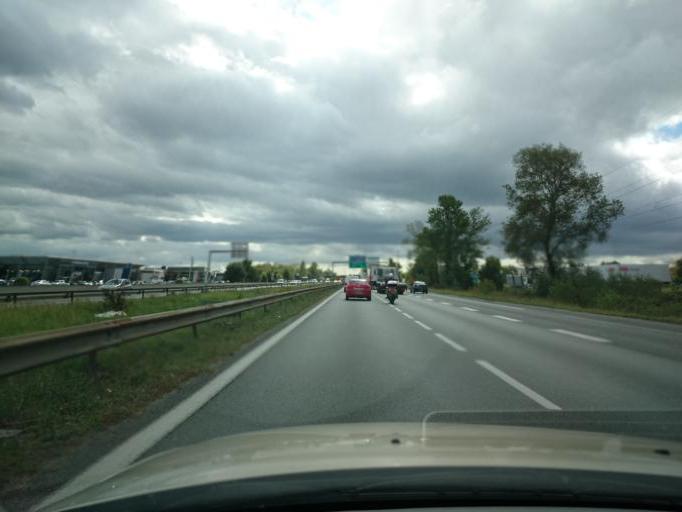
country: FR
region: Aquitaine
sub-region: Departement de la Gironde
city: Le Haillan
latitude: 44.8475
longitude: -0.6696
